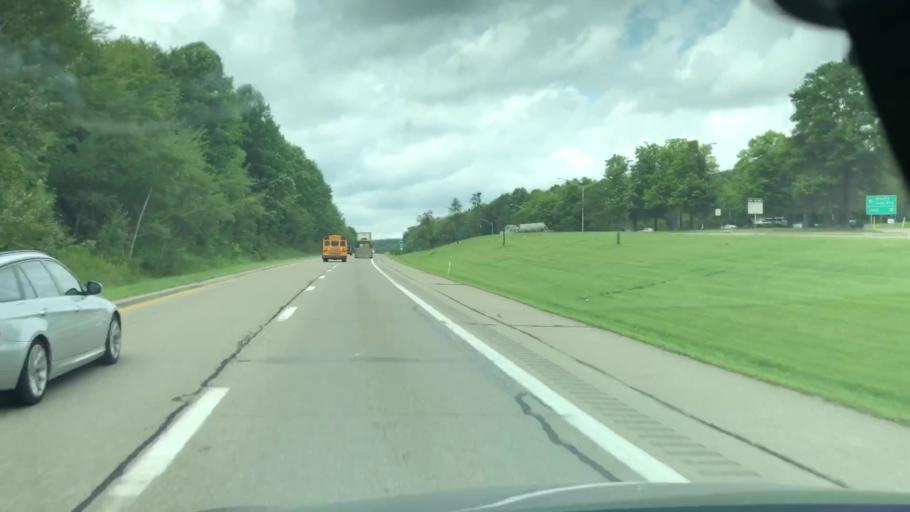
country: US
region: Pennsylvania
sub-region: Erie County
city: Edinboro
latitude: 41.8406
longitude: -80.1759
